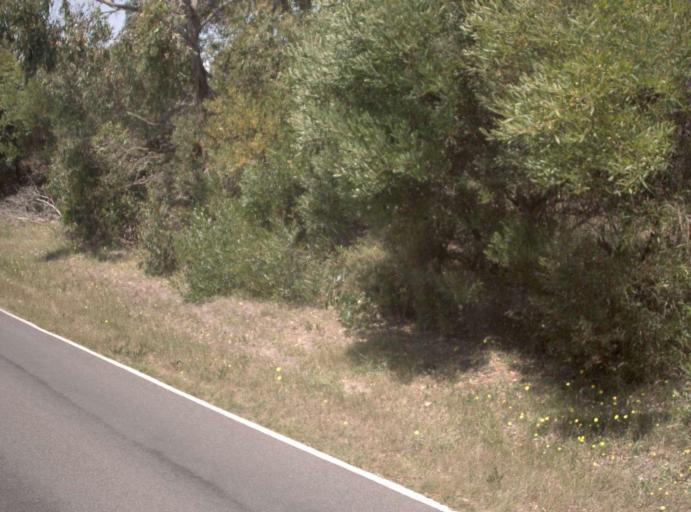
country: AU
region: Victoria
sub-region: Bass Coast
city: North Wonthaggi
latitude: -38.6724
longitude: 145.8618
